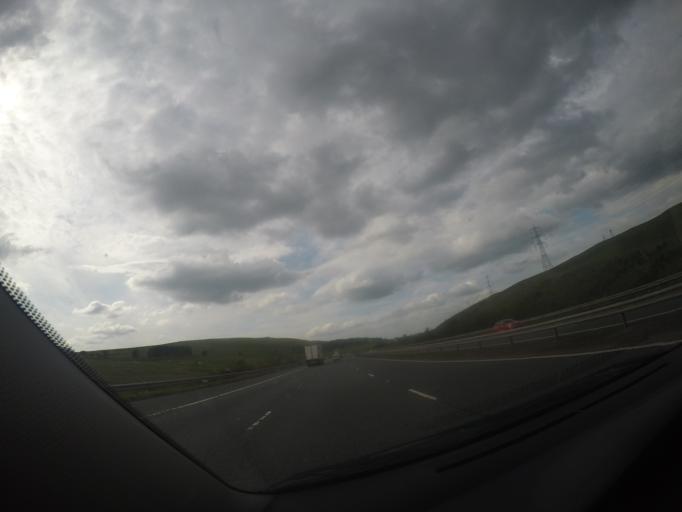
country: GB
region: Scotland
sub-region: South Lanarkshire
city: Douglas
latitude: 55.5458
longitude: -3.7971
